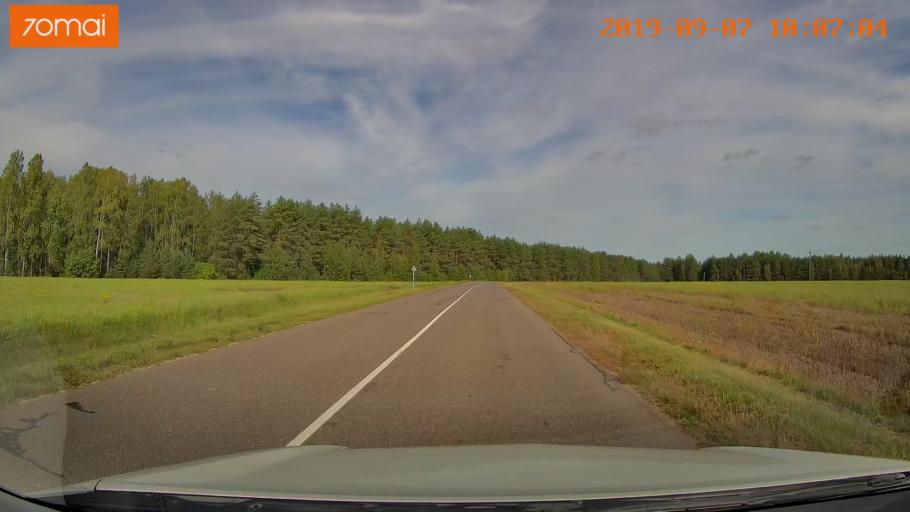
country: BY
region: Grodnenskaya
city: Voranava
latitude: 54.0702
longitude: 25.3966
